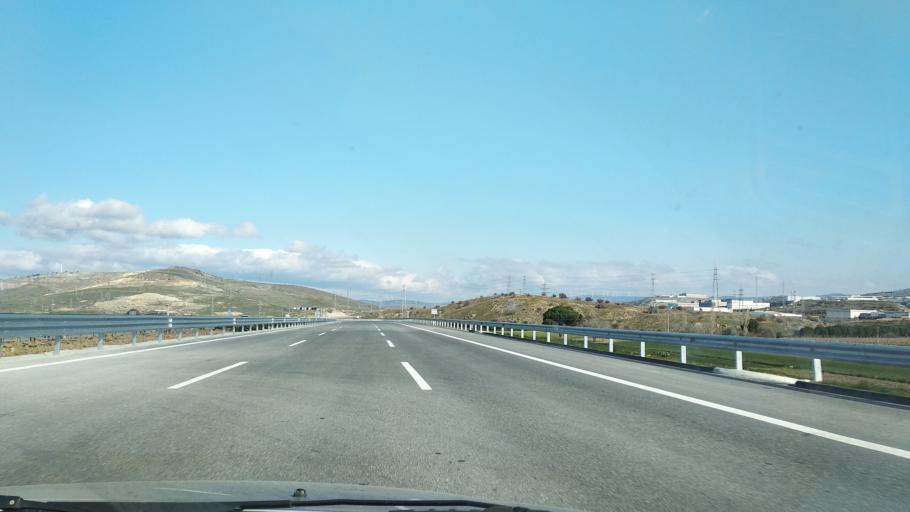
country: TR
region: Izmir
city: Aliaga
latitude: 38.8138
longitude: 27.0247
